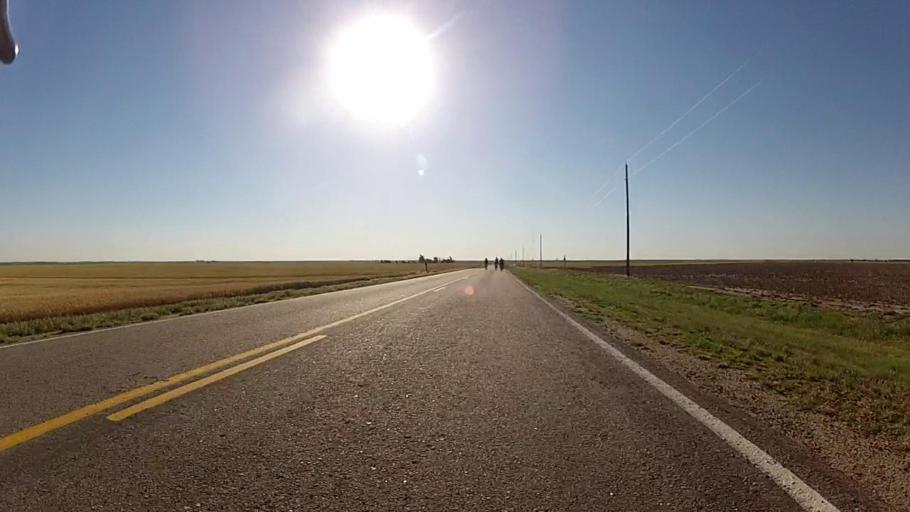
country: US
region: Kansas
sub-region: Ford County
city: Dodge City
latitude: 37.6466
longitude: -99.8622
